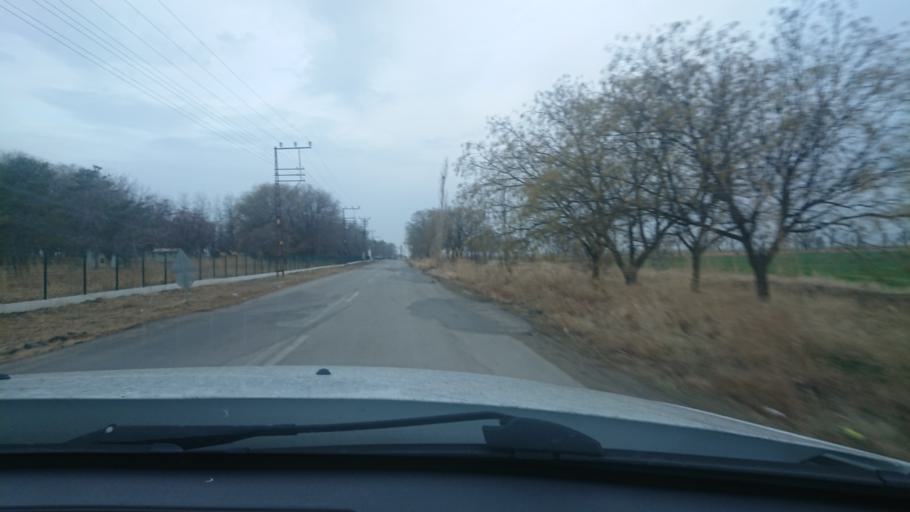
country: TR
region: Aksaray
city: Yesilova
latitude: 38.4603
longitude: 33.8429
